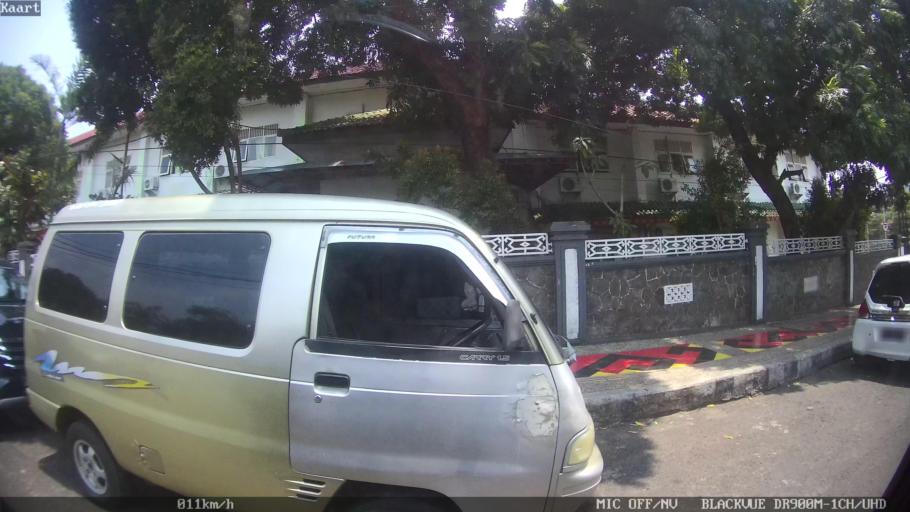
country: ID
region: Lampung
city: Bandarlampung
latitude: -5.4251
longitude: 105.2690
